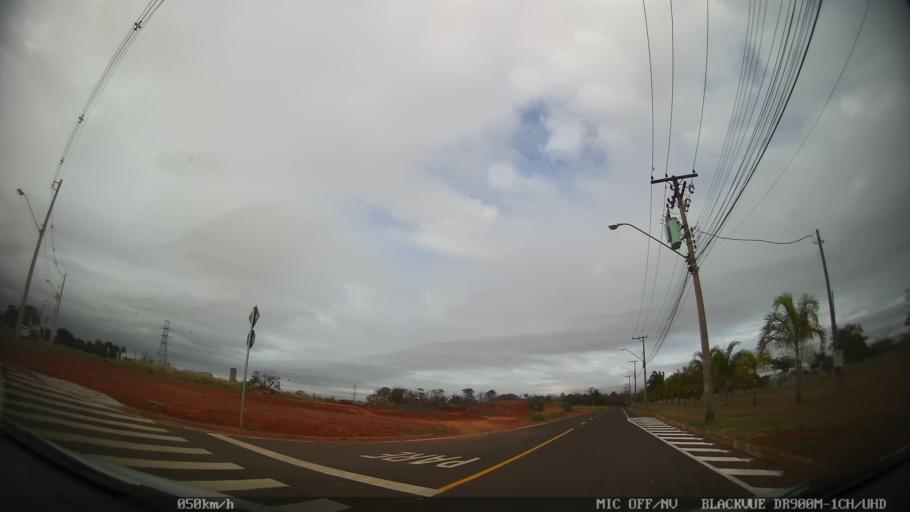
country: BR
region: Sao Paulo
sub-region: Sao Jose Do Rio Preto
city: Sao Jose do Rio Preto
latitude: -20.8267
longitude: -49.4170
